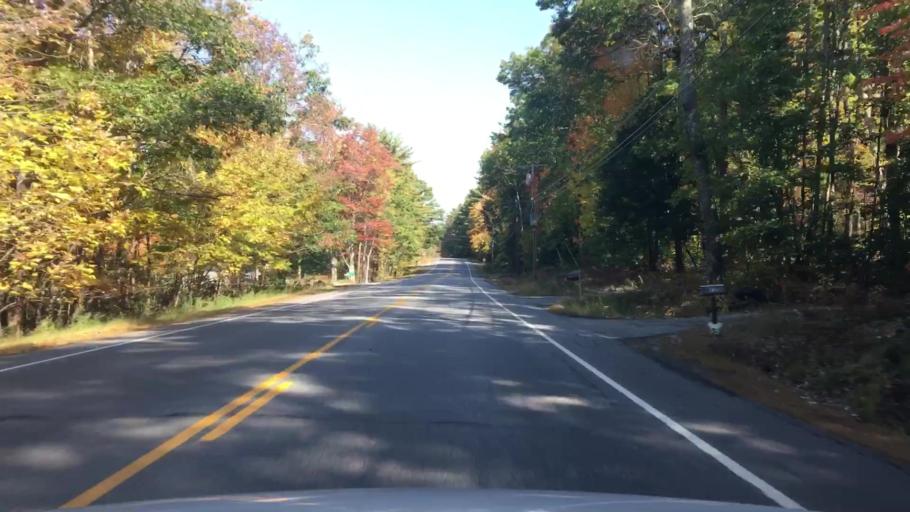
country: US
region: Maine
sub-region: Sagadahoc County
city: Topsham
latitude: 44.0019
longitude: -69.9499
